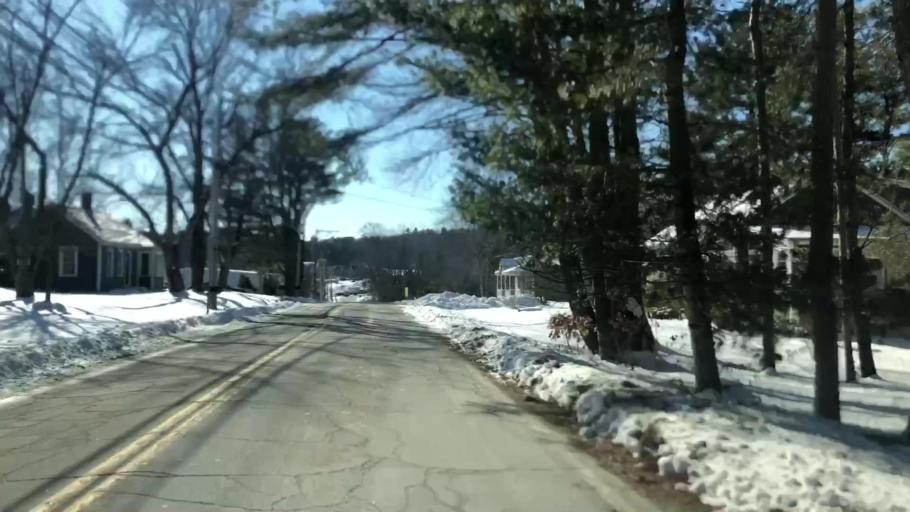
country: US
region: New Hampshire
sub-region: Hillsborough County
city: Bedford
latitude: 42.9409
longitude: -71.5228
